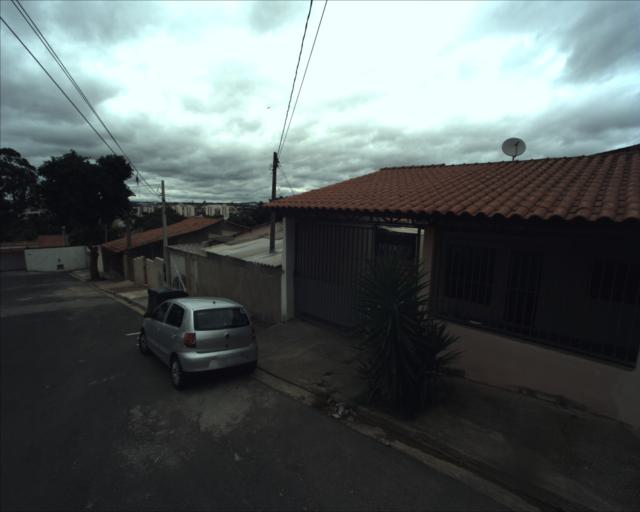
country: BR
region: Sao Paulo
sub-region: Sorocaba
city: Sorocaba
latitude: -23.4784
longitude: -47.4620
